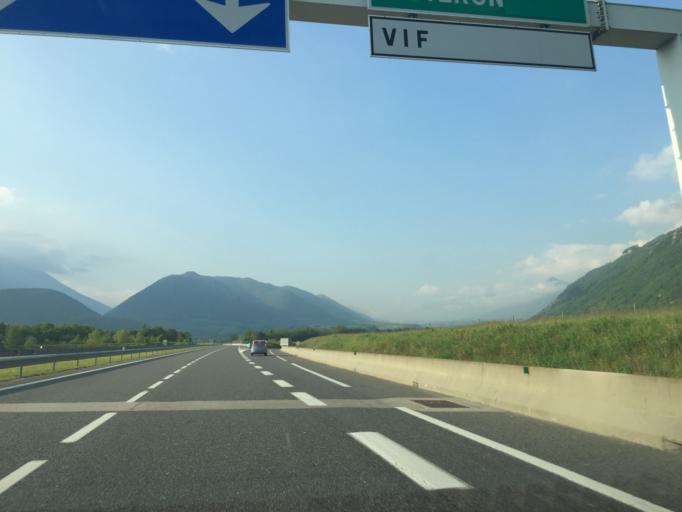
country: FR
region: Rhone-Alpes
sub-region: Departement de l'Isere
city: Allieres-et-Risset
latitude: 45.0778
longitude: 5.6794
